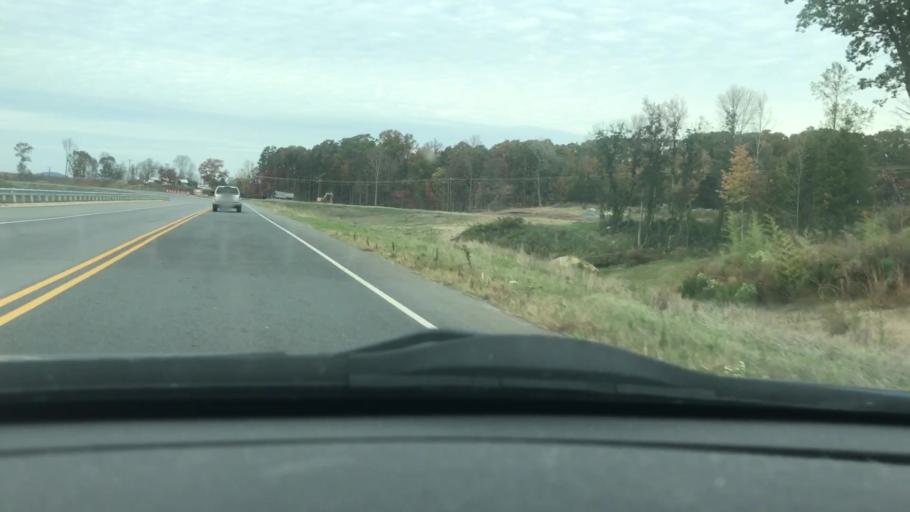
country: US
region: North Carolina
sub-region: Randolph County
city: Asheboro
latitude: 35.6992
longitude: -79.8724
